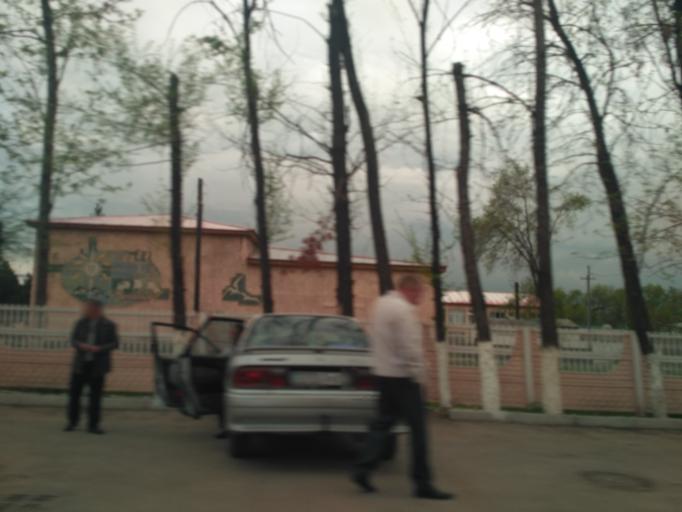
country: KZ
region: Almaty Oblysy
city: Burunday
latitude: 43.2110
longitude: 76.3208
